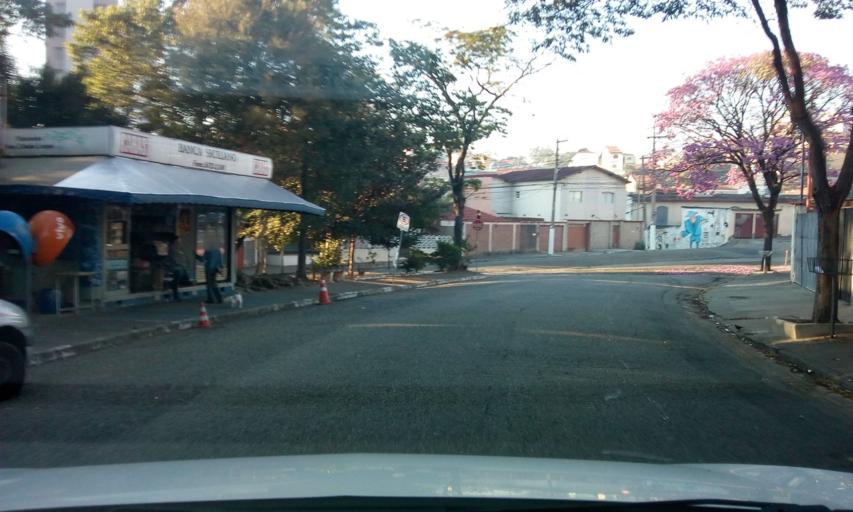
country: BR
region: Sao Paulo
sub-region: Sao Paulo
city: Sao Paulo
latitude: -23.5352
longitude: -46.6964
